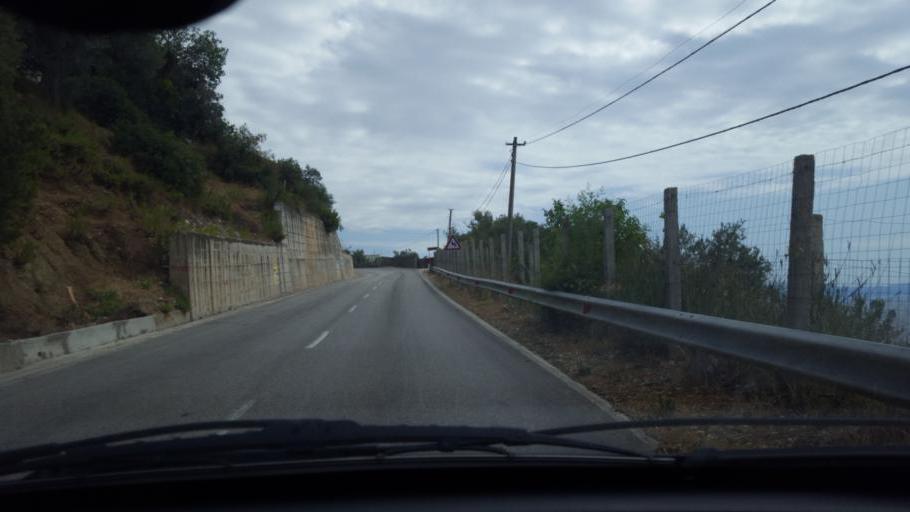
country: AL
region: Vlore
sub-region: Rrethi i Sarandes
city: Lukove
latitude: 40.0593
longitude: 19.8590
